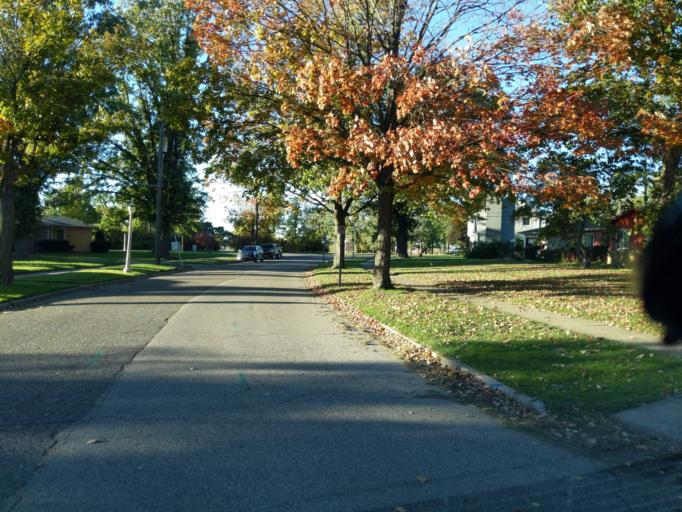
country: US
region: Michigan
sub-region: Ingham County
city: Edgemont Park
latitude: 42.7284
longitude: -84.5792
